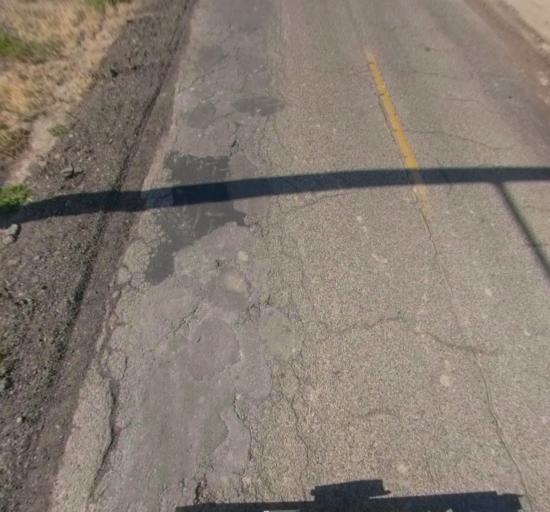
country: US
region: California
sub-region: Madera County
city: Parkwood
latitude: 36.8693
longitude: -120.1284
